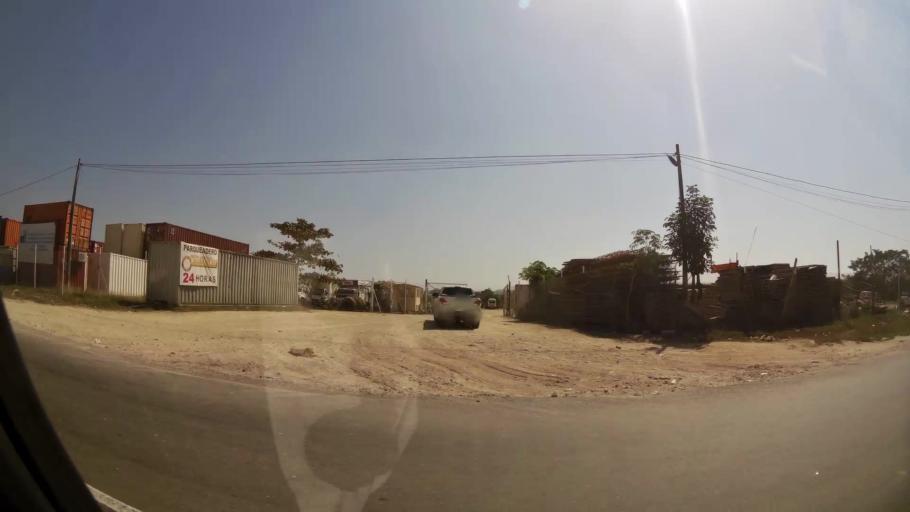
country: CO
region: Bolivar
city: Cartagena
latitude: 10.3844
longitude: -75.4500
